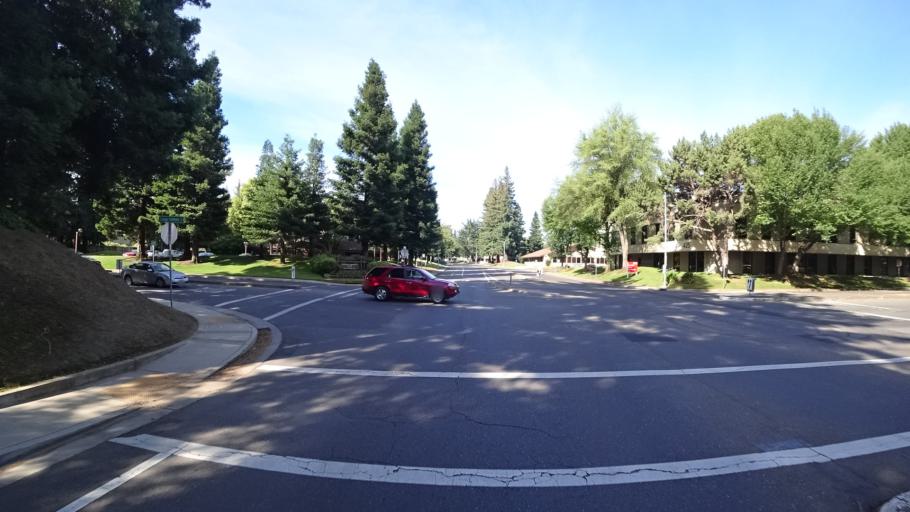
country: US
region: California
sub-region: Sacramento County
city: Arden-Arcade
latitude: 38.5702
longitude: -121.4171
